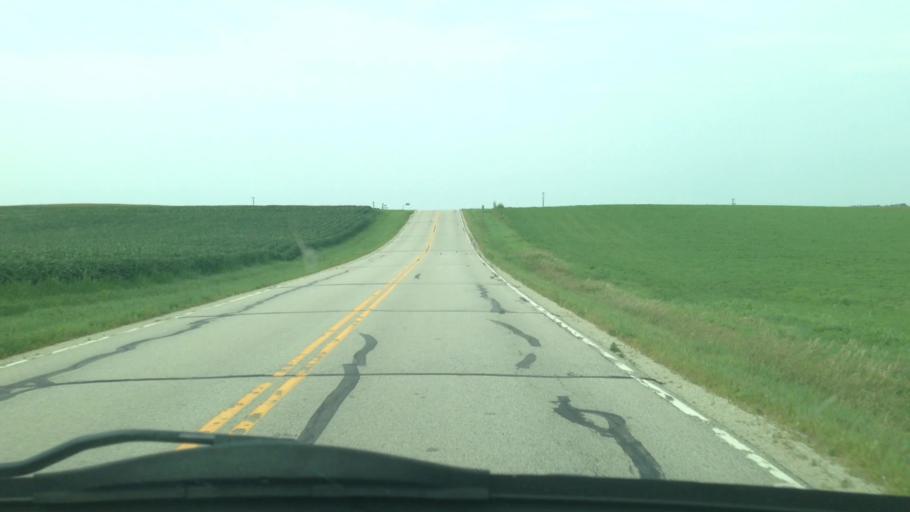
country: US
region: Minnesota
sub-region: Fillmore County
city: Preston
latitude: 43.7865
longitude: -91.9498
